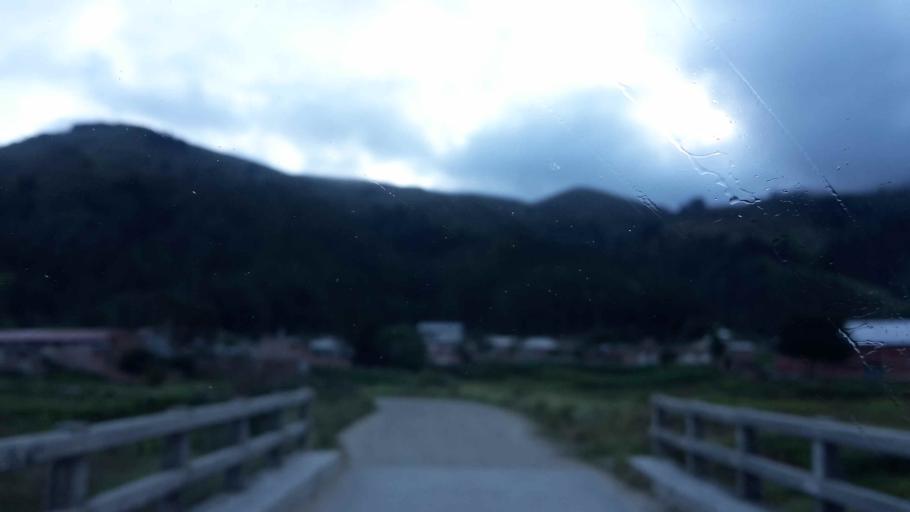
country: BO
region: Cochabamba
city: Colomi
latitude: -17.2727
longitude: -65.9240
